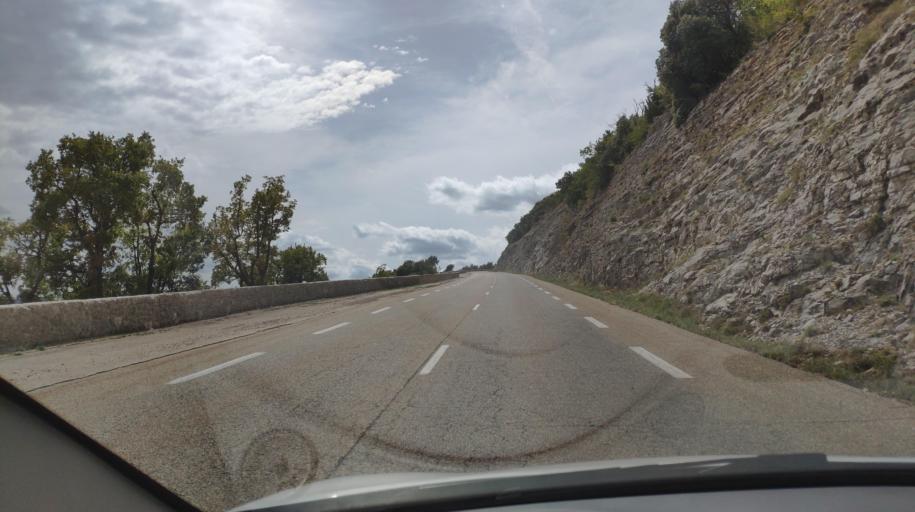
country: FR
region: Provence-Alpes-Cote d'Azur
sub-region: Departement du Vaucluse
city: Sault
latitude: 44.0841
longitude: 5.3664
